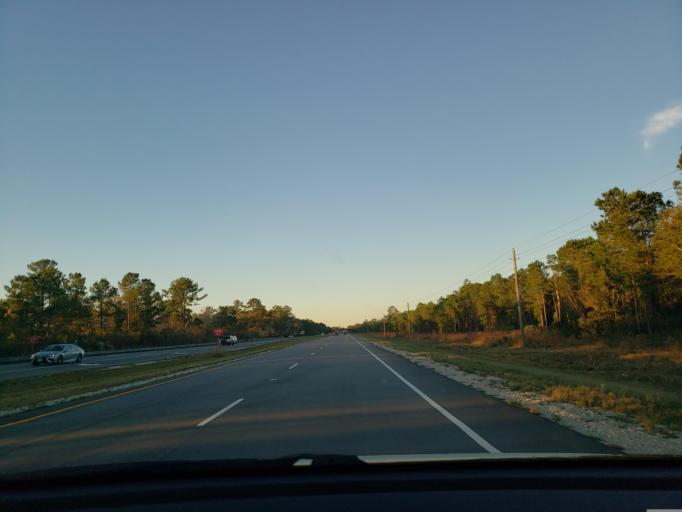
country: US
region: North Carolina
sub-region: Onslow County
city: Sneads Ferry
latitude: 34.5993
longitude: -77.4813
